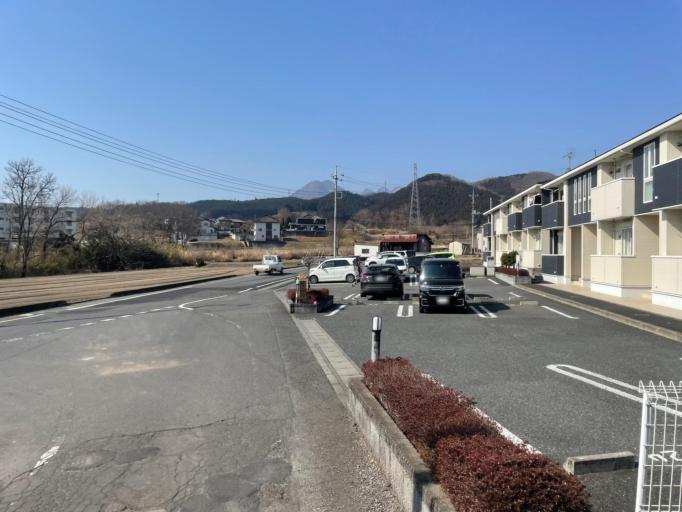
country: JP
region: Gunma
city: Shibukawa
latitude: 36.5121
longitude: 138.9973
